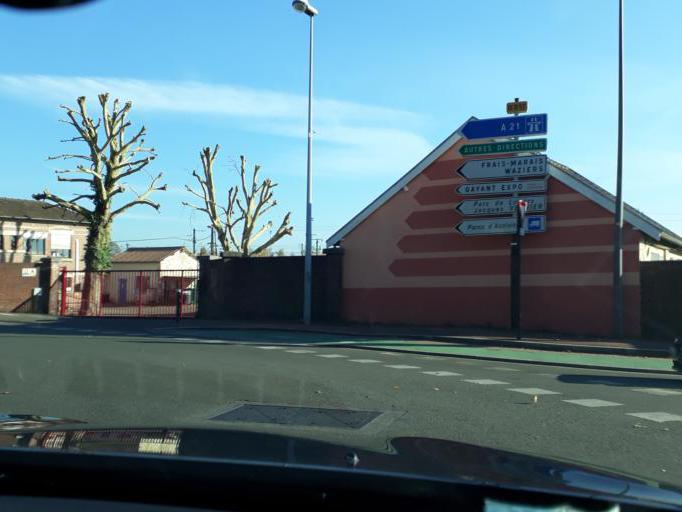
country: FR
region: Nord-Pas-de-Calais
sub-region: Departement du Nord
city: Douai
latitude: 50.3776
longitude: 3.0895
